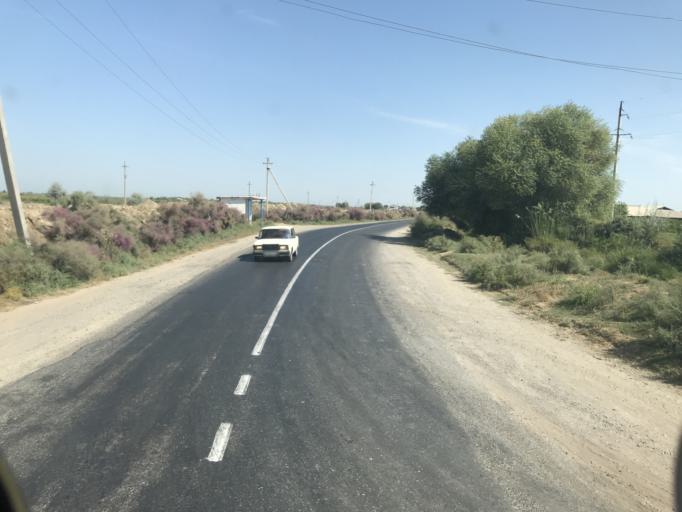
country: KZ
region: Ongtustik Qazaqstan
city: Myrzakent
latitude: 40.7247
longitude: 68.5347
